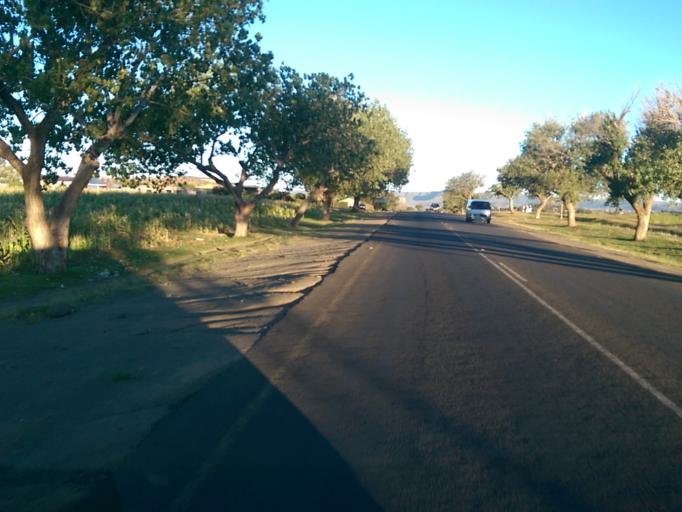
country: LS
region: Maseru
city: Maseru
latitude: -29.4086
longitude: 27.6102
